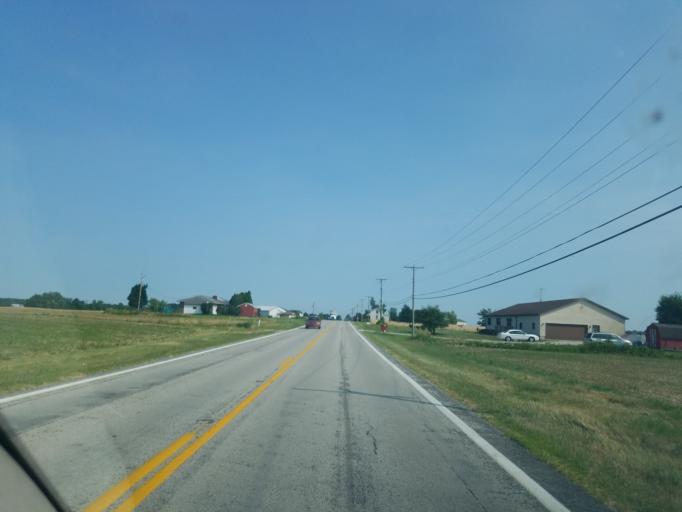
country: US
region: Ohio
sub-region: Wyandot County
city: Carey
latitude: 41.0463
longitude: -83.3137
